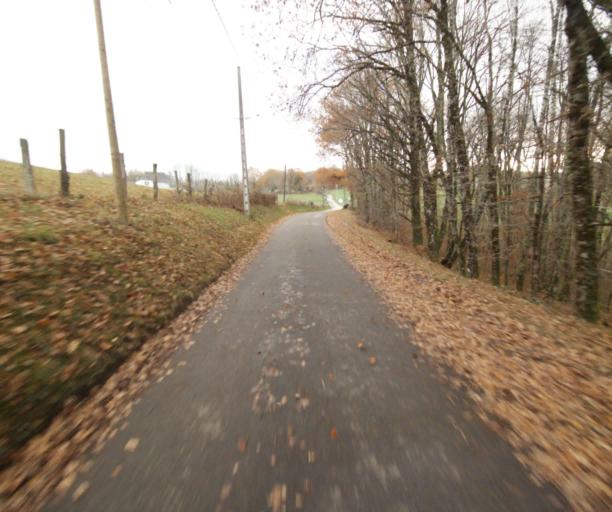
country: FR
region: Limousin
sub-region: Departement de la Correze
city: Laguenne
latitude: 45.2268
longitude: 1.7829
